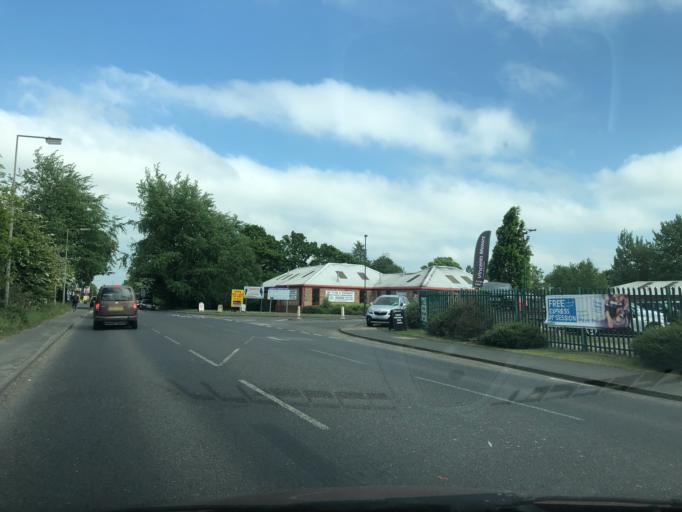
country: GB
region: England
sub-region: North Yorkshire
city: Catterick Garrison
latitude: 54.3796
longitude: -1.6814
